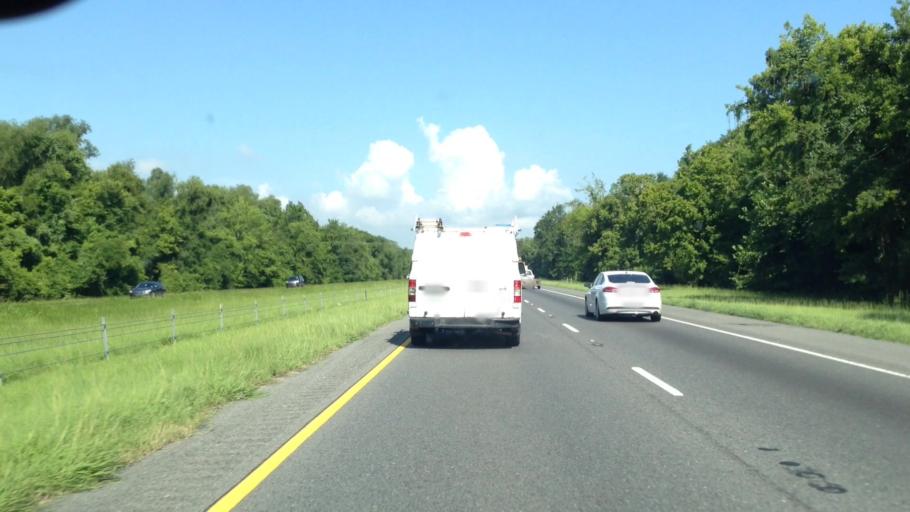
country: US
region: Louisiana
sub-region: Ascension Parish
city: Sorrento
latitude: 30.1637
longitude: -90.8482
